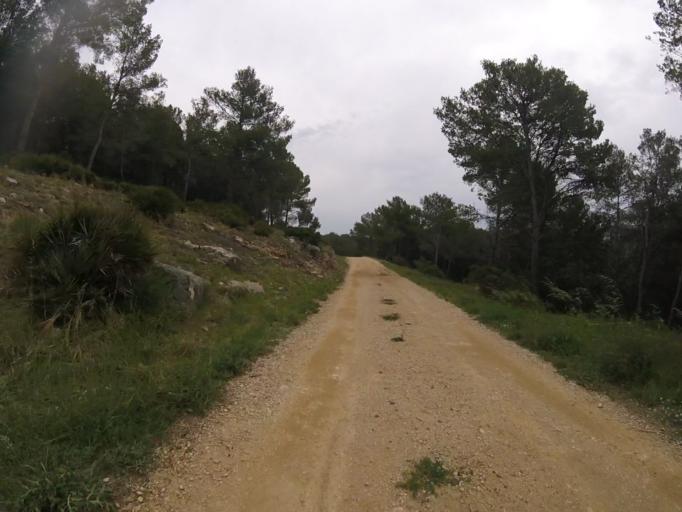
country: ES
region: Valencia
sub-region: Provincia de Castello
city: Alcala de Xivert
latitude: 40.3068
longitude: 0.2559
